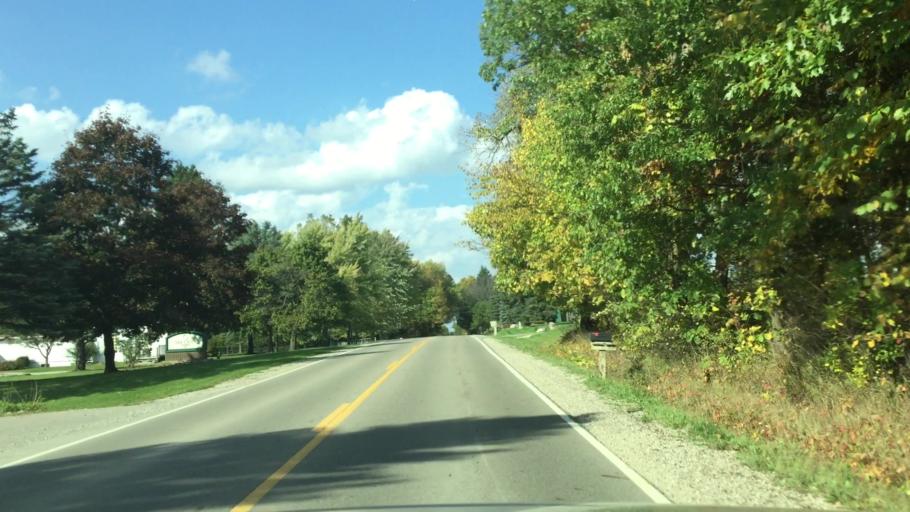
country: US
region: Michigan
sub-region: Oakland County
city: Milford
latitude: 42.6545
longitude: -83.7006
